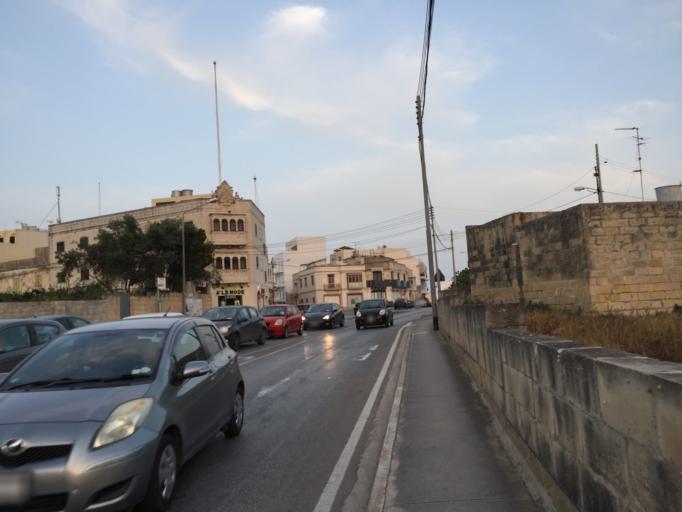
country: MT
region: Haz-Zabbar
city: Zabbar
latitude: 35.8723
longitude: 14.5321
